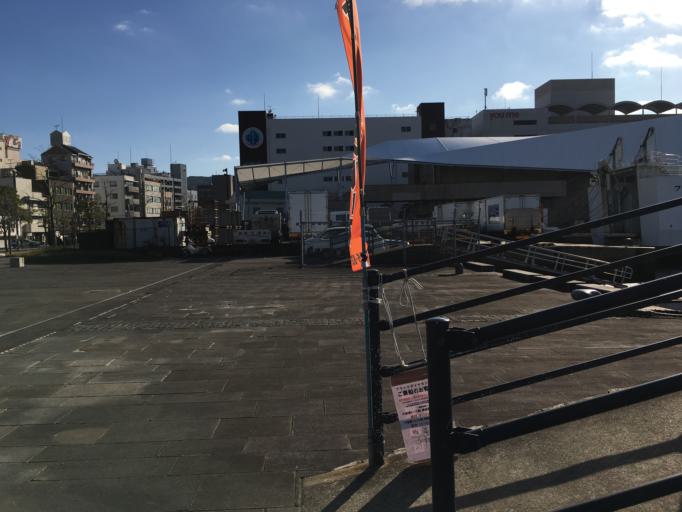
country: JP
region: Nagasaki
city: Nagasaki-shi
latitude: 32.7479
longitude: 129.8708
